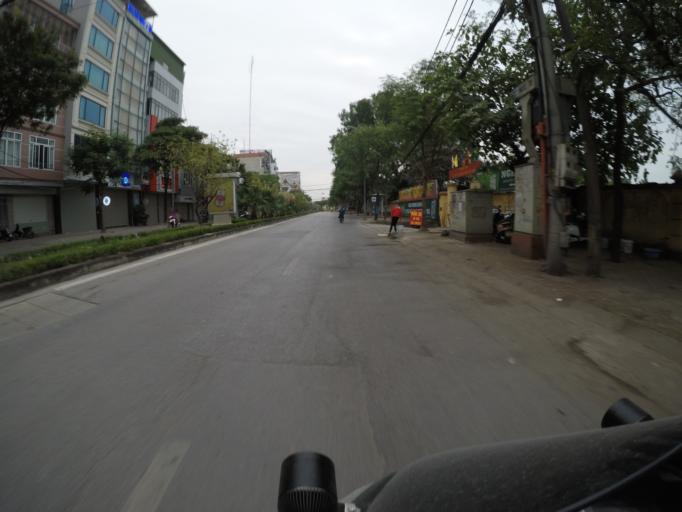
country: VN
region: Ha Noi
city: Tay Ho
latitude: 21.0654
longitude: 105.8102
